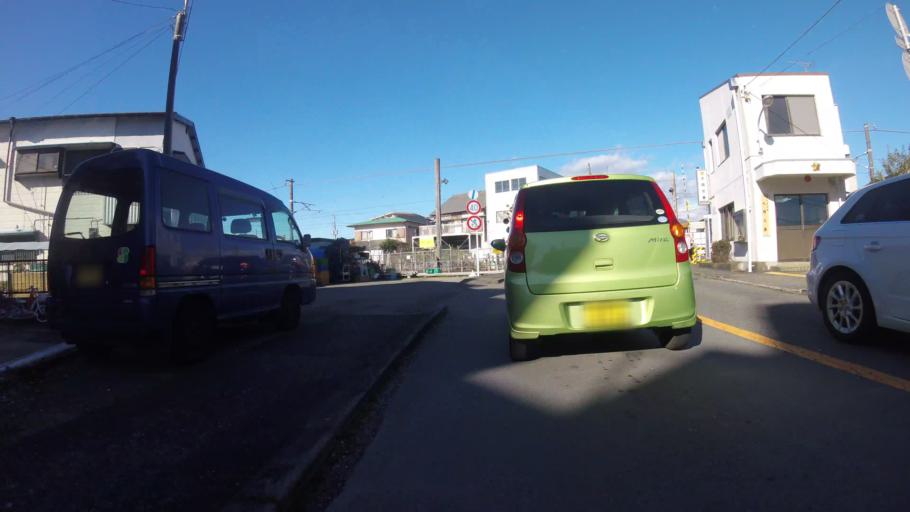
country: JP
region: Shizuoka
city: Numazu
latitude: 35.1154
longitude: 138.8808
